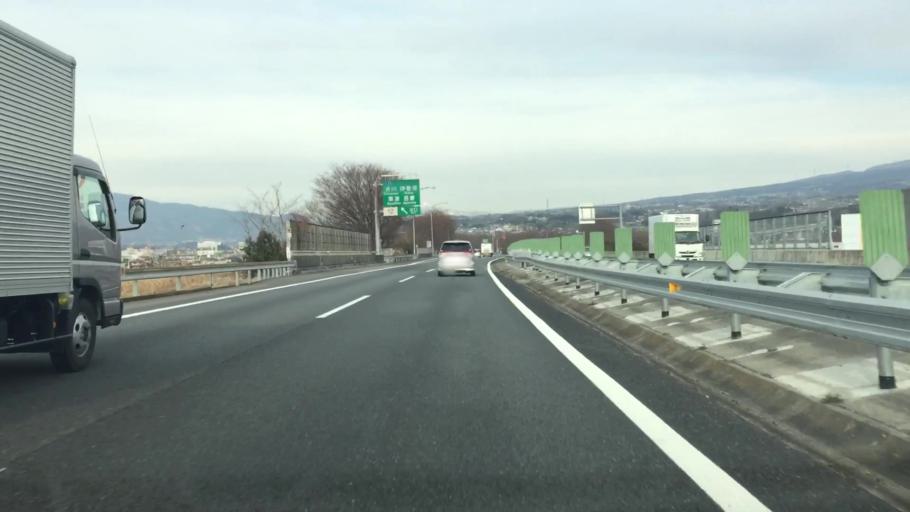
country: JP
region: Gunma
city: Shibukawa
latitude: 36.4719
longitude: 139.0132
